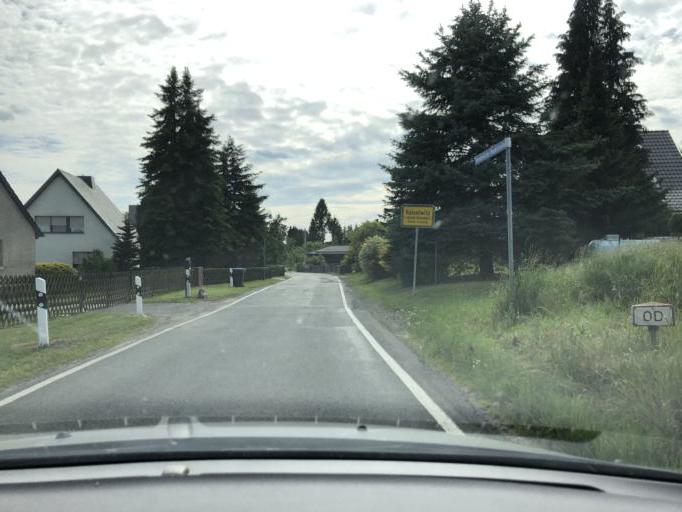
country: DE
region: Saxony
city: Ostrau
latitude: 51.2016
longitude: 12.8238
